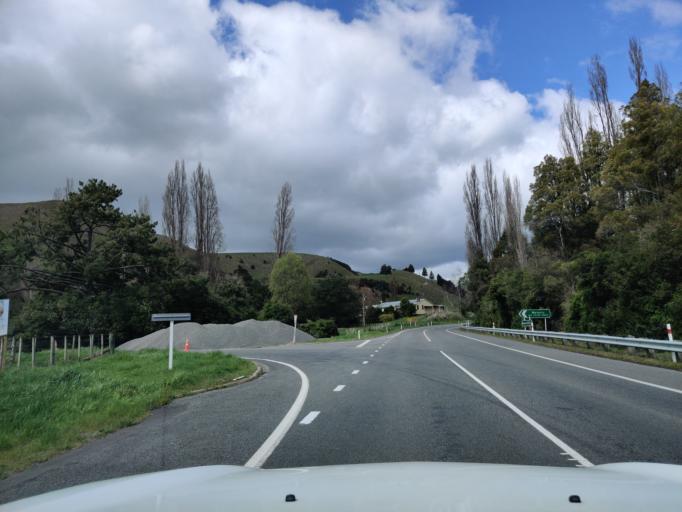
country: NZ
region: Manawatu-Wanganui
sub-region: Ruapehu District
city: Waiouru
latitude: -39.6521
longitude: 175.3277
